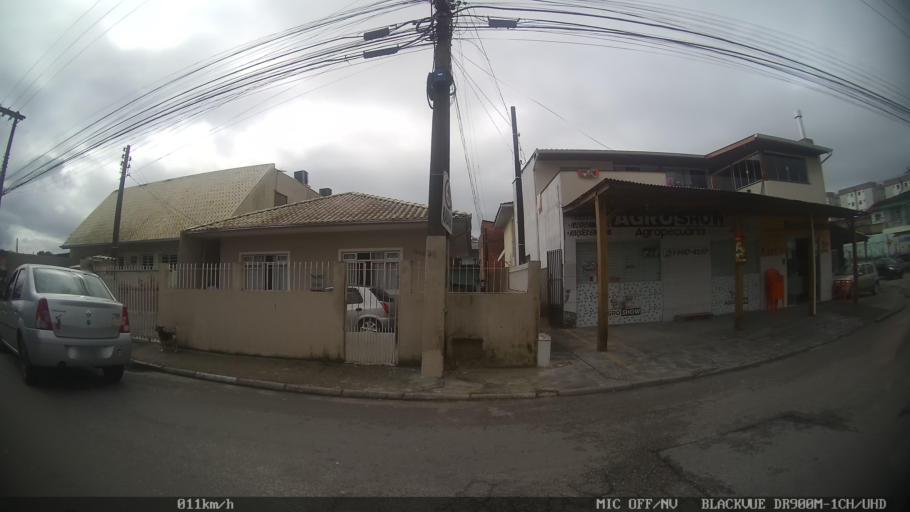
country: BR
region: Santa Catarina
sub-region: Biguacu
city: Biguacu
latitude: -27.5338
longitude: -48.6402
